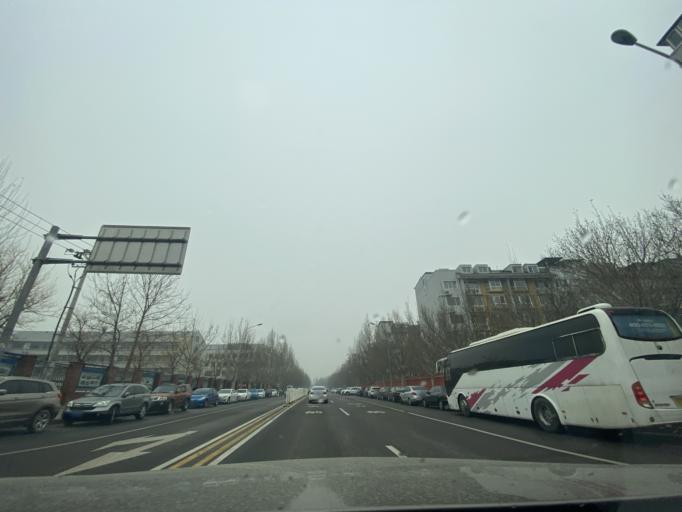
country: CN
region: Beijing
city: Sijiqing
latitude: 39.9629
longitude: 116.2418
